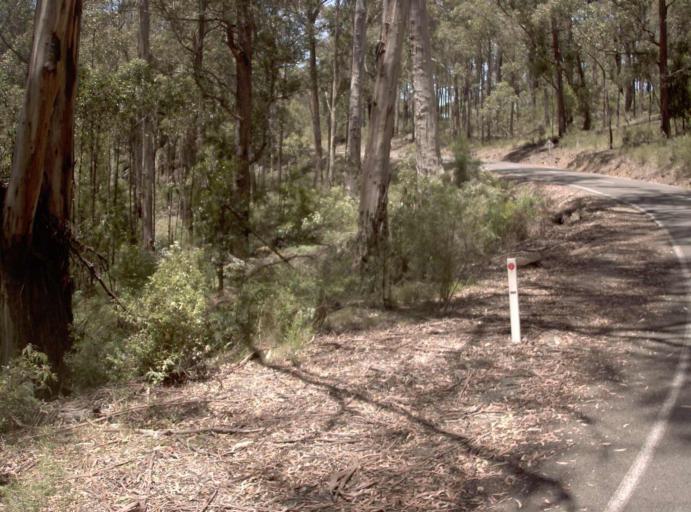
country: AU
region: Victoria
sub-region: East Gippsland
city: Lakes Entrance
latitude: -37.6046
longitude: 147.8820
